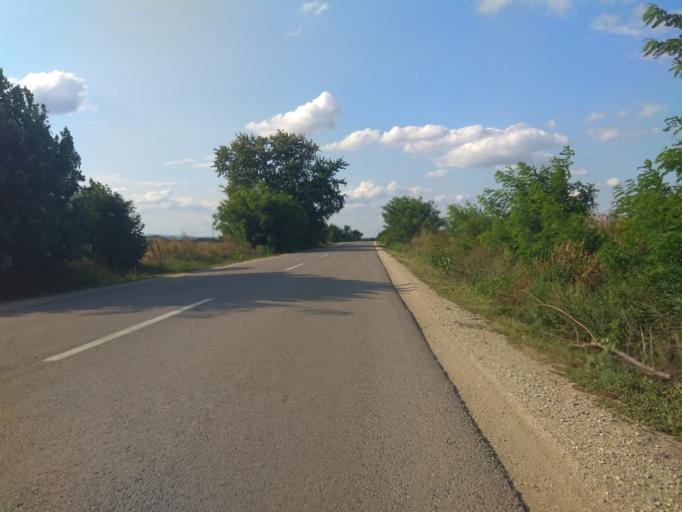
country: HU
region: Borsod-Abauj-Zemplen
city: Hejobaba
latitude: 47.8988
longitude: 20.8913
